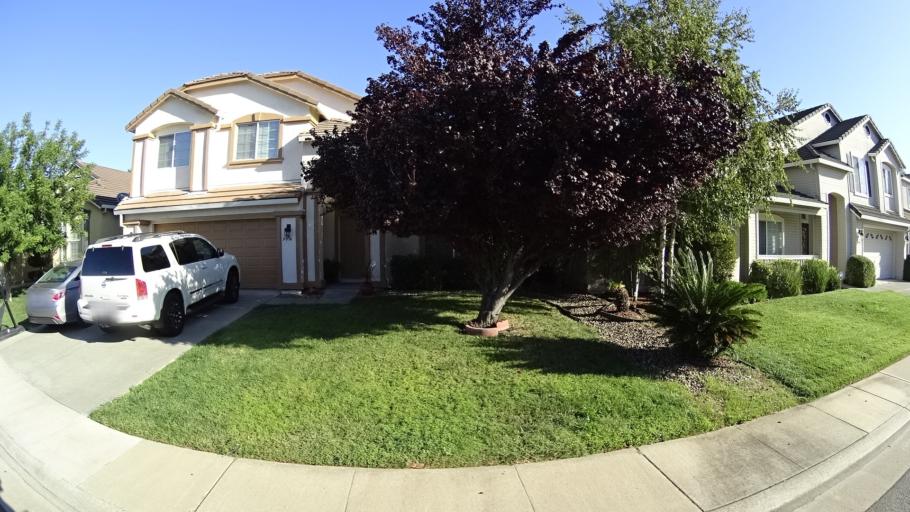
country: US
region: California
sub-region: Sacramento County
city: Laguna
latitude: 38.4294
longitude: -121.4506
